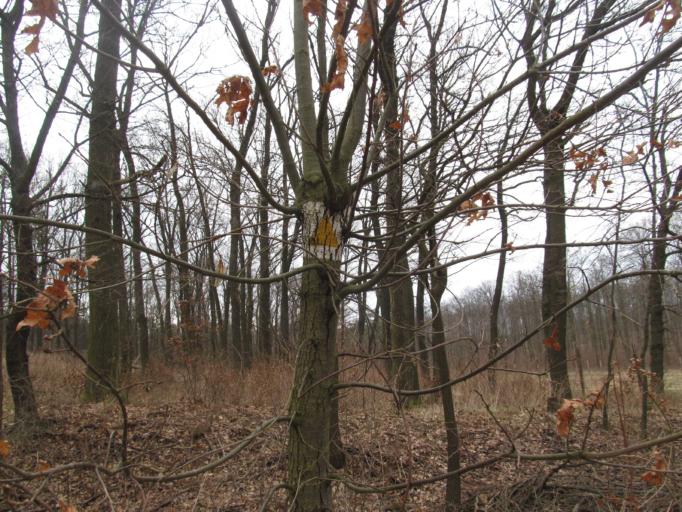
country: HU
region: Gyor-Moson-Sopron
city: Pannonhalma
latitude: 47.5330
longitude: 17.7739
